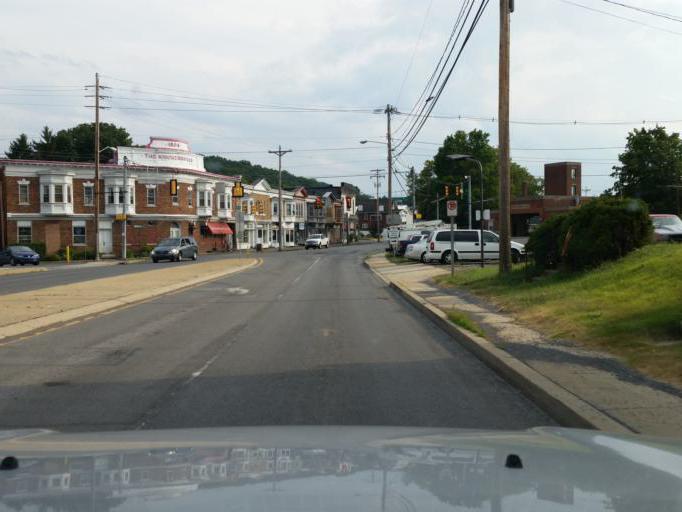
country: US
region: Pennsylvania
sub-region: Blair County
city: Lakemont
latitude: 40.4878
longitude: -78.4144
